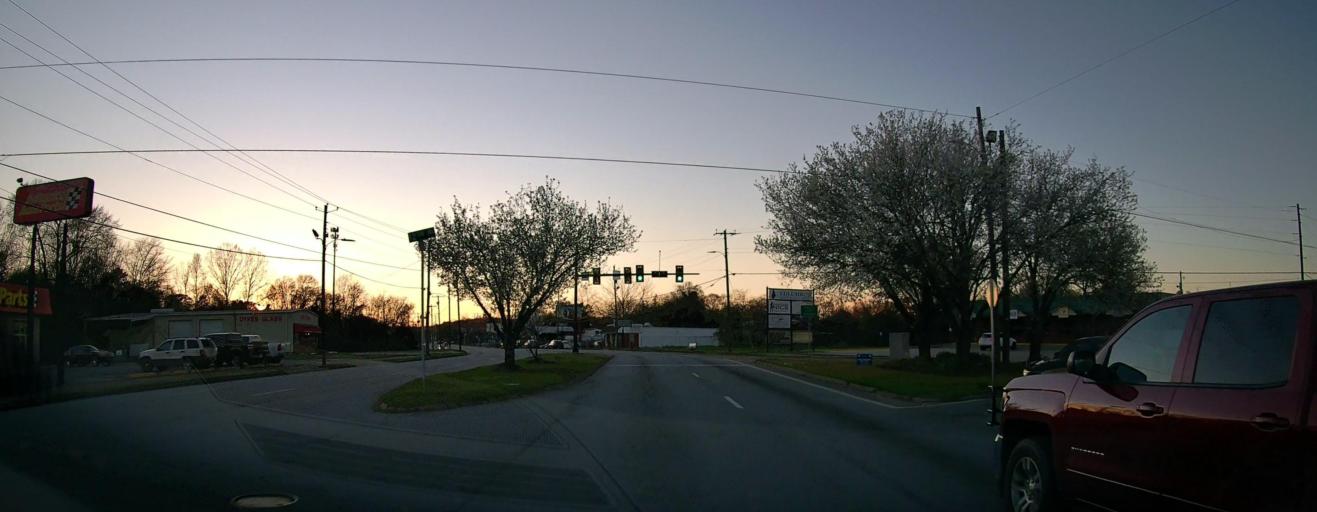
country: US
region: Alabama
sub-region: Russell County
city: Phenix City
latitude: 32.4723
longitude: -85.0089
